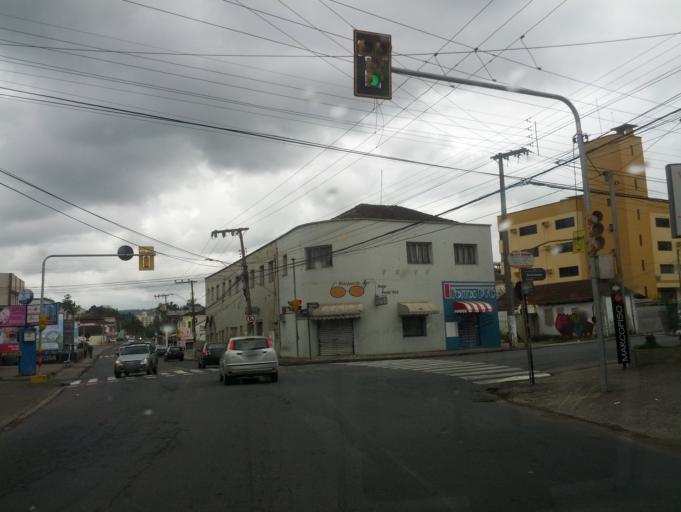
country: BR
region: Santa Catarina
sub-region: Blumenau
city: Blumenau
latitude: -26.9112
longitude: -49.0921
